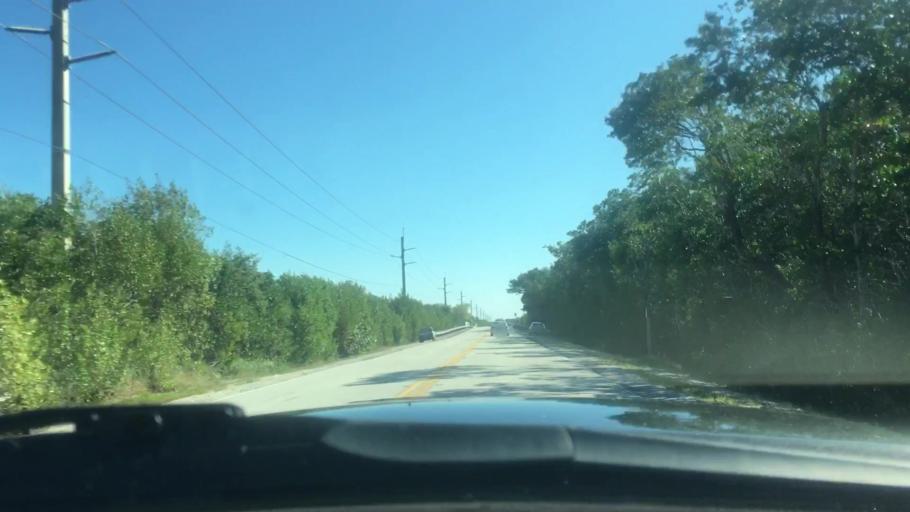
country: US
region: Florida
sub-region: Monroe County
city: North Key Largo
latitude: 25.2832
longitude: -80.3561
